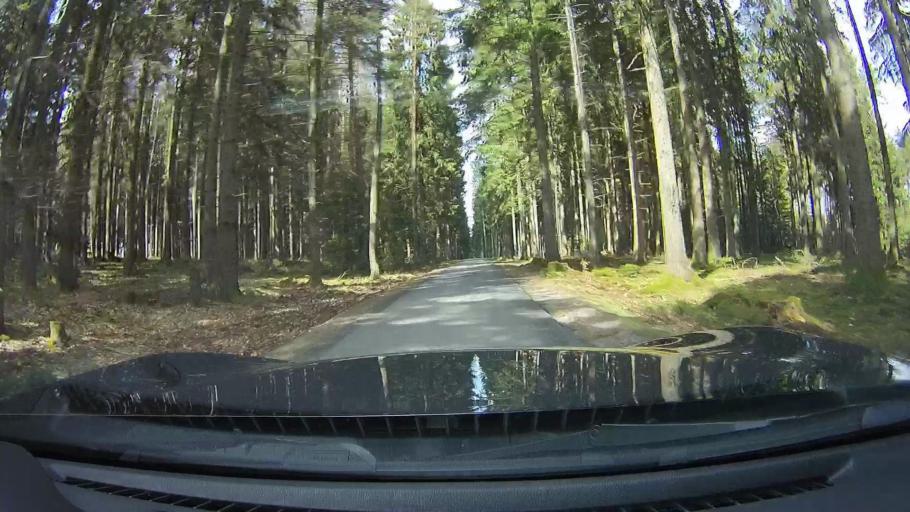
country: DE
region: Hesse
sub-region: Regierungsbezirk Darmstadt
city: Hesseneck
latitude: 49.5936
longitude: 9.0859
